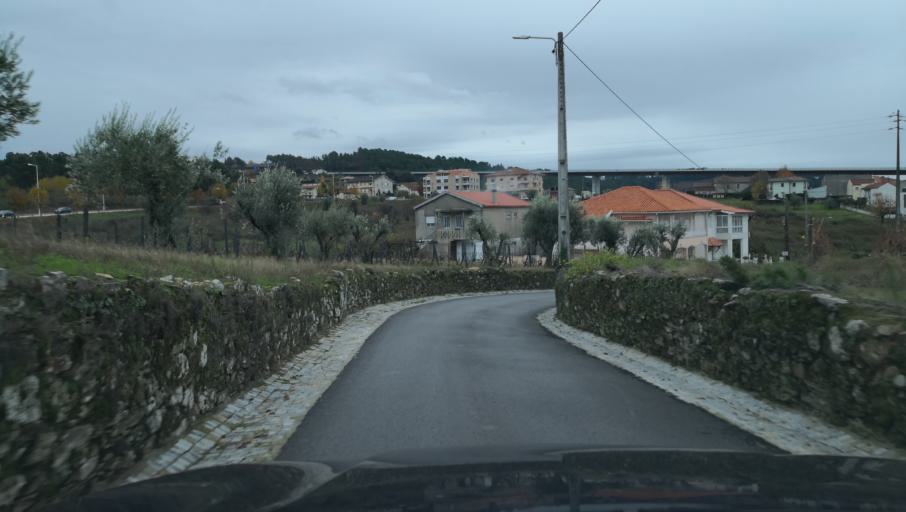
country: PT
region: Vila Real
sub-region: Vila Real
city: Vila Real
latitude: 41.2830
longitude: -7.7394
